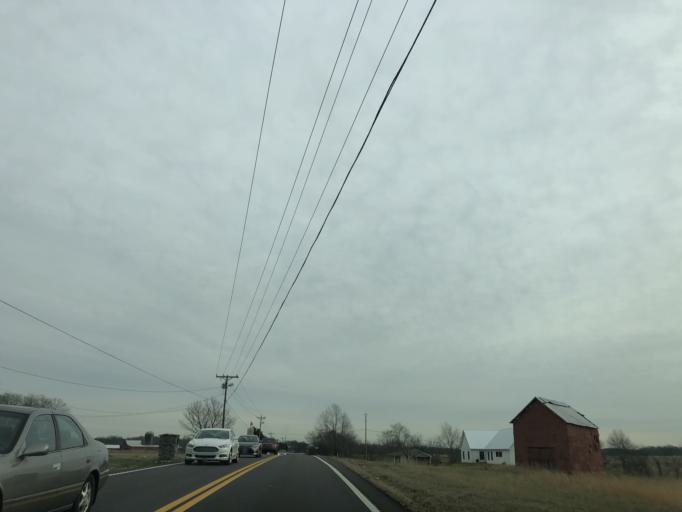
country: US
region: Tennessee
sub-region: Sumner County
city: White House
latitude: 36.4729
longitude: -86.7033
